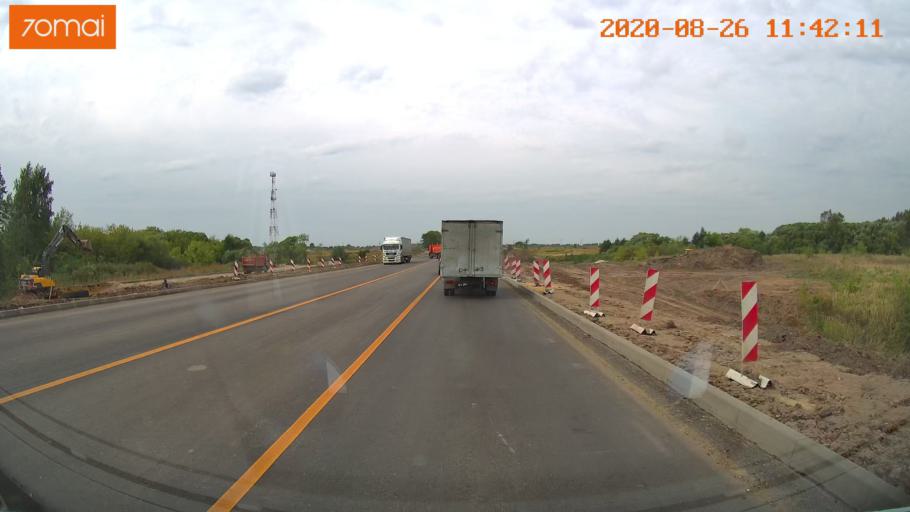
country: RU
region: Rjazan
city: Shilovo
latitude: 54.2968
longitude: 40.6980
